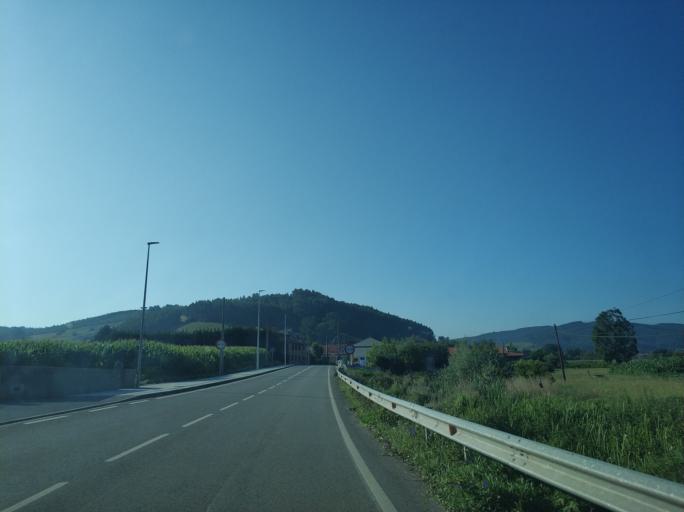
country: ES
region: Cantabria
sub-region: Provincia de Cantabria
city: Polanco
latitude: 43.3708
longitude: -3.9606
